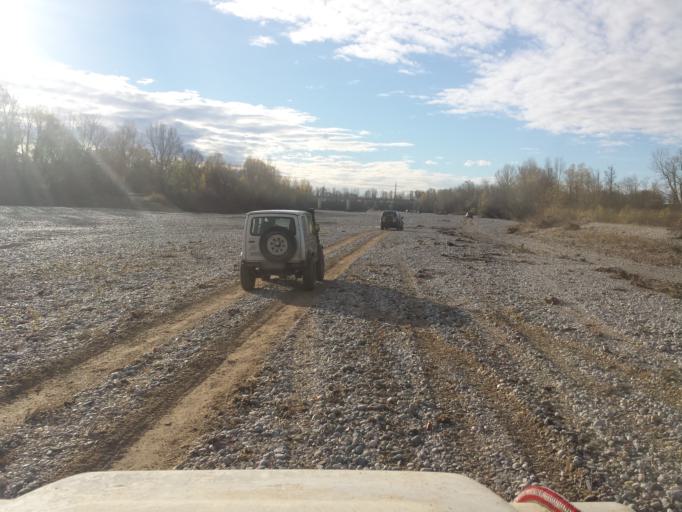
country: IT
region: Friuli Venezia Giulia
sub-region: Provincia di Udine
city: San Vito al Torre
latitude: 45.8988
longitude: 13.4036
